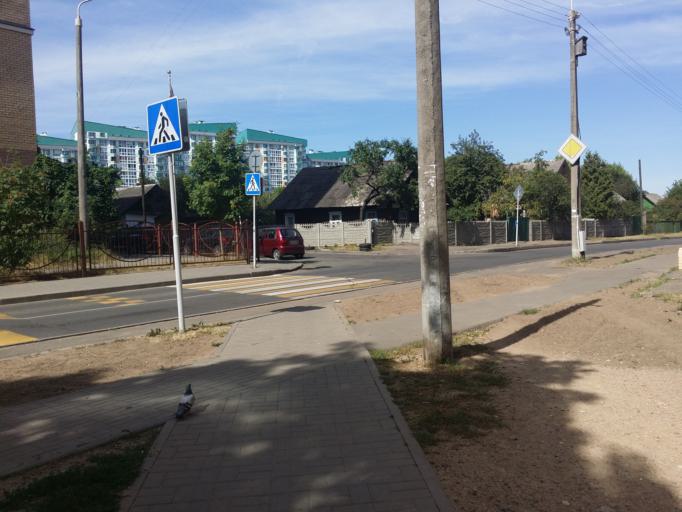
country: BY
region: Minsk
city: Minsk
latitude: 53.9410
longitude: 27.6003
